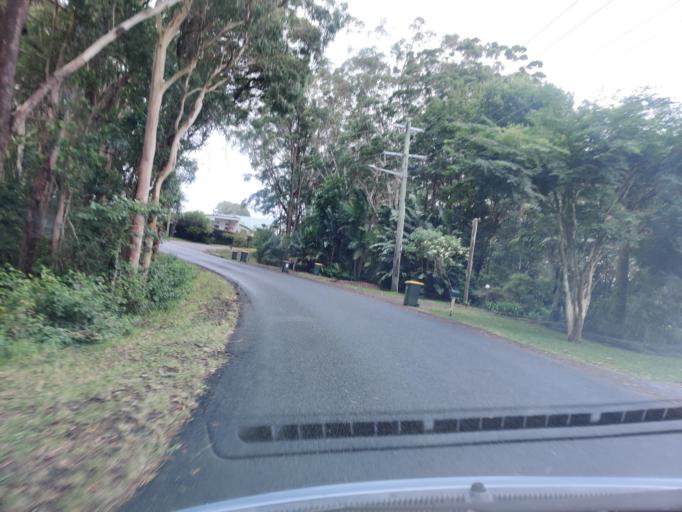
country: AU
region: New South Wales
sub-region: Great Lakes
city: Forster
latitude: -32.3839
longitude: 152.5039
